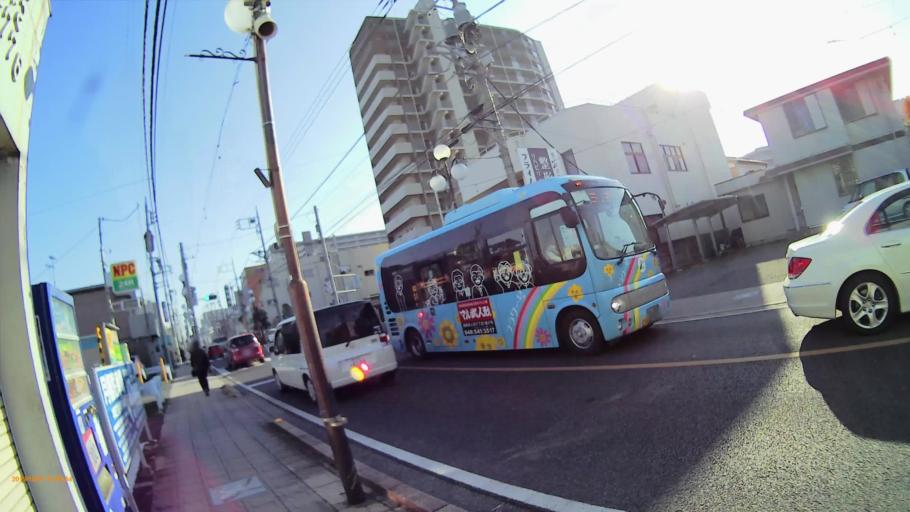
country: JP
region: Saitama
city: Konosu
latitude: 36.0620
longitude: 139.5108
